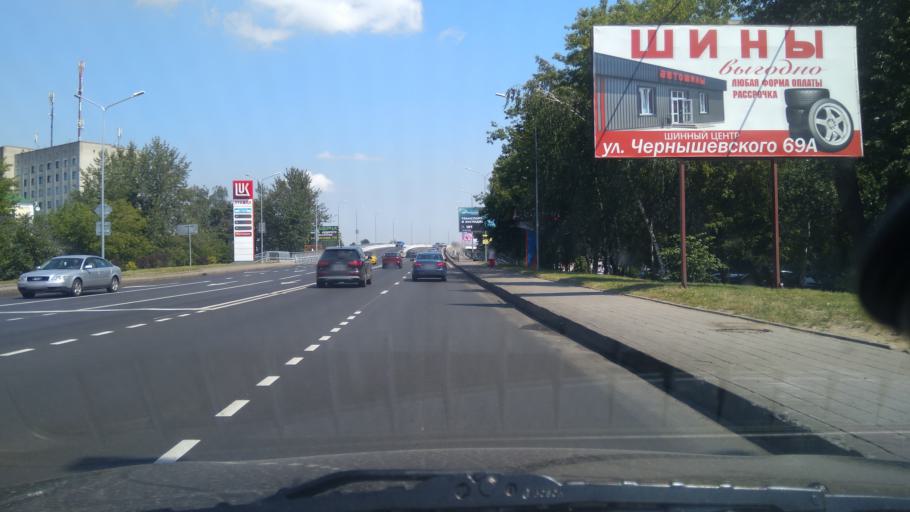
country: BY
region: Brest
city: Baranovichi
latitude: 53.1307
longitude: 26.0347
